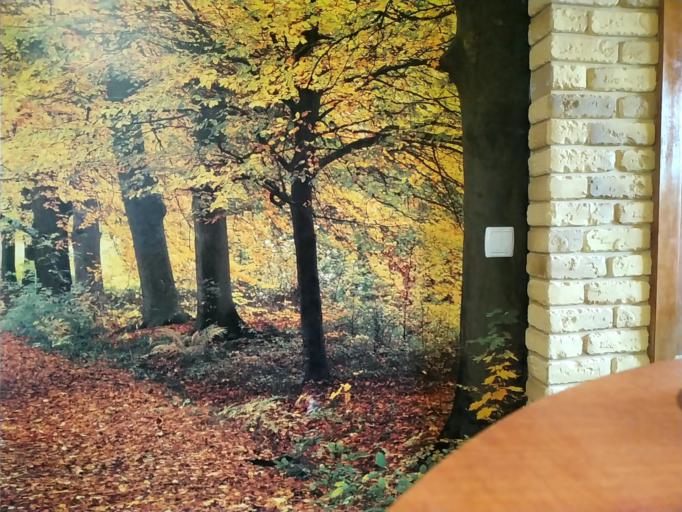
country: RU
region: Novgorod
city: Opechenskiy Posad
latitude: 58.2701
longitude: 34.0111
